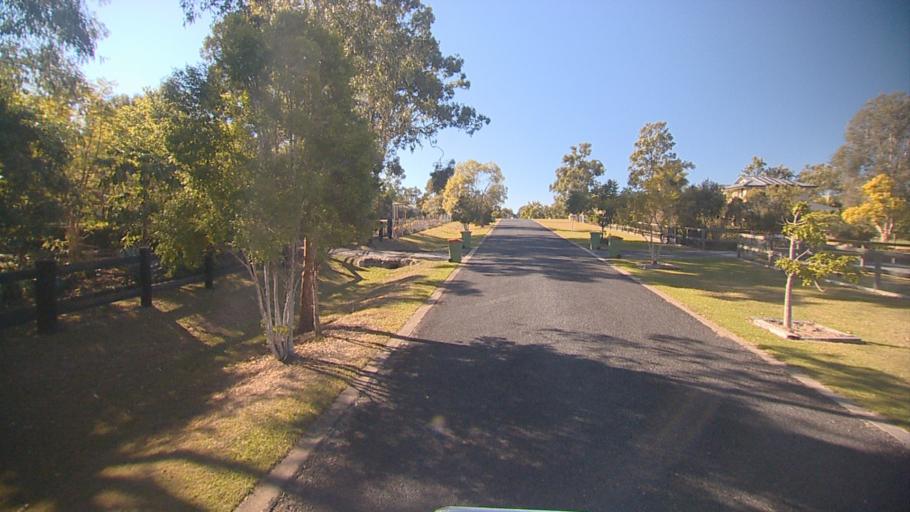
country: AU
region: Queensland
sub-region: Logan
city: North Maclean
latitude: -27.7340
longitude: 152.9689
